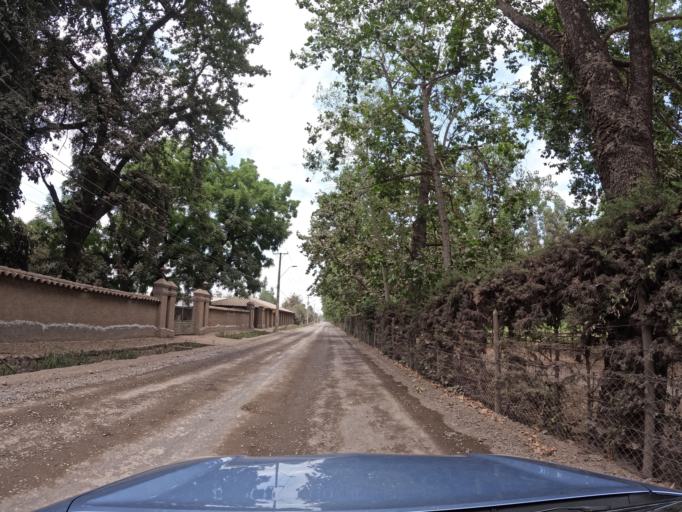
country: CL
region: O'Higgins
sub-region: Provincia de Colchagua
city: Chimbarongo
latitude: -34.7374
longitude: -70.9761
